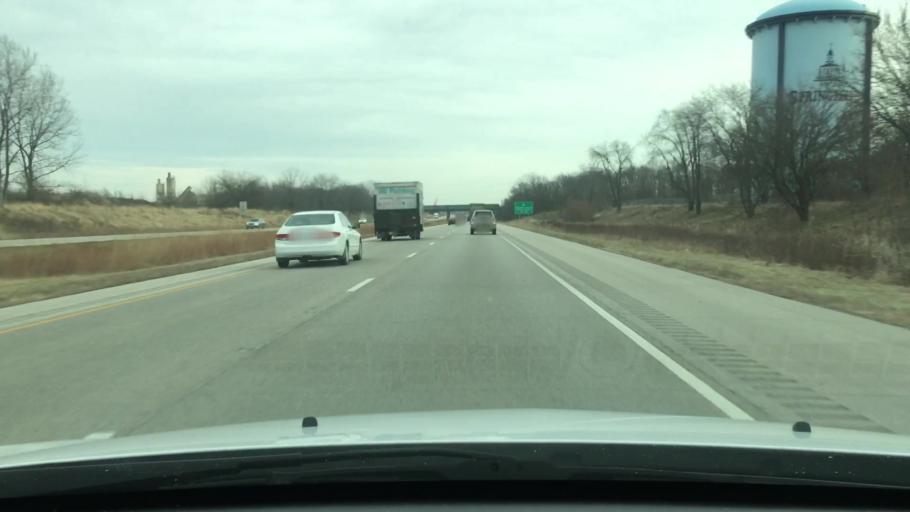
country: US
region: Illinois
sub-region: Sangamon County
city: Jerome
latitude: 39.7463
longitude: -89.7184
